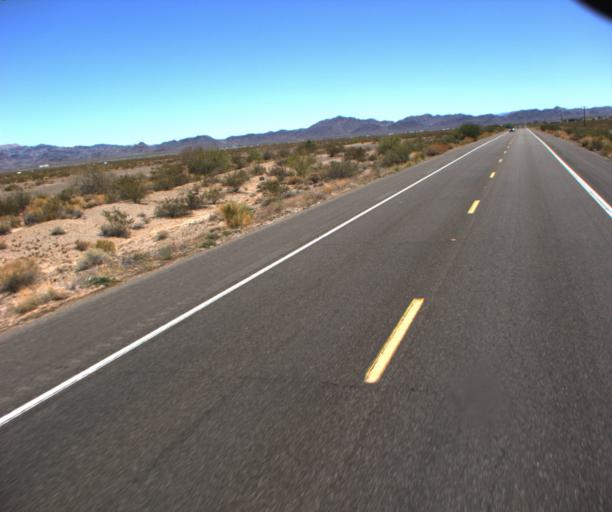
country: US
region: Arizona
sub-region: La Paz County
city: Salome
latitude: 33.7140
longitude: -113.7927
